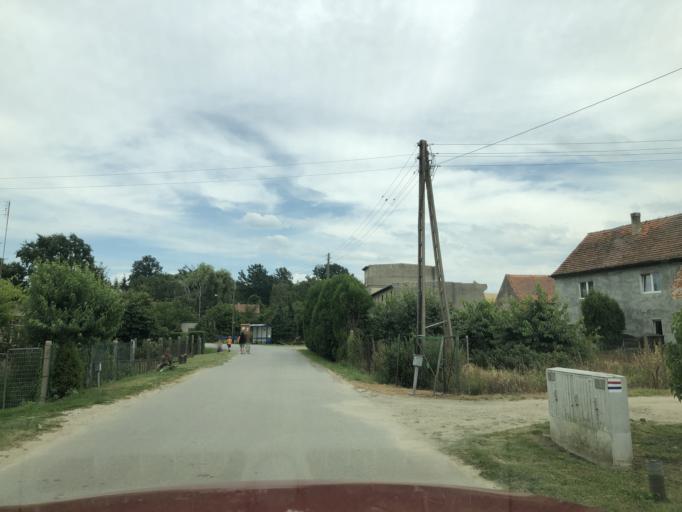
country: PL
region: Lower Silesian Voivodeship
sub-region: Powiat trzebnicki
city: Trzebnica
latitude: 51.3211
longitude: 17.0032
